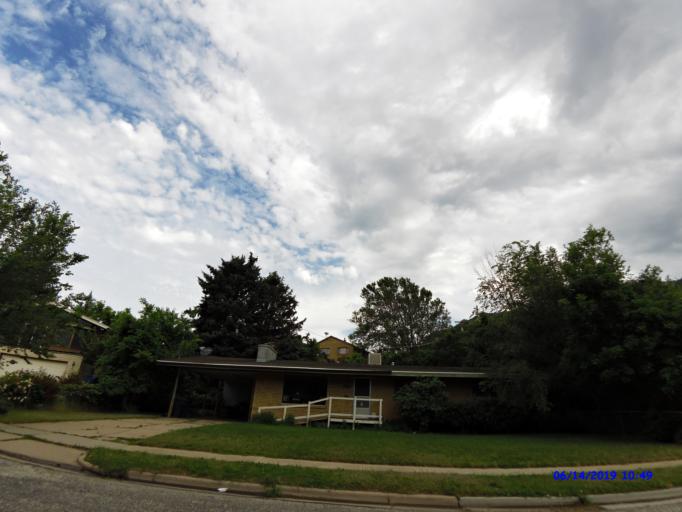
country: US
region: Utah
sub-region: Weber County
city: Ogden
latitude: 41.2450
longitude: -111.9440
